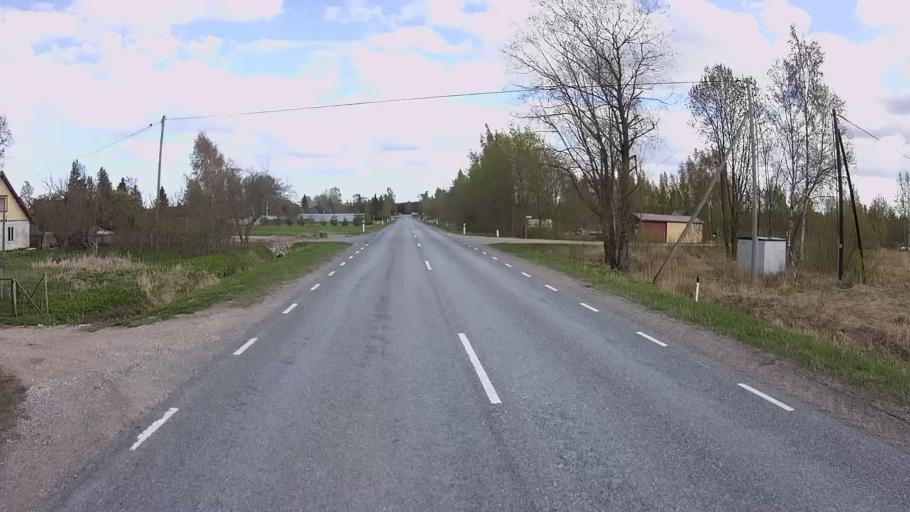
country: EE
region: Jogevamaa
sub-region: Mustvee linn
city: Mustvee
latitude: 58.7835
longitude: 26.9715
